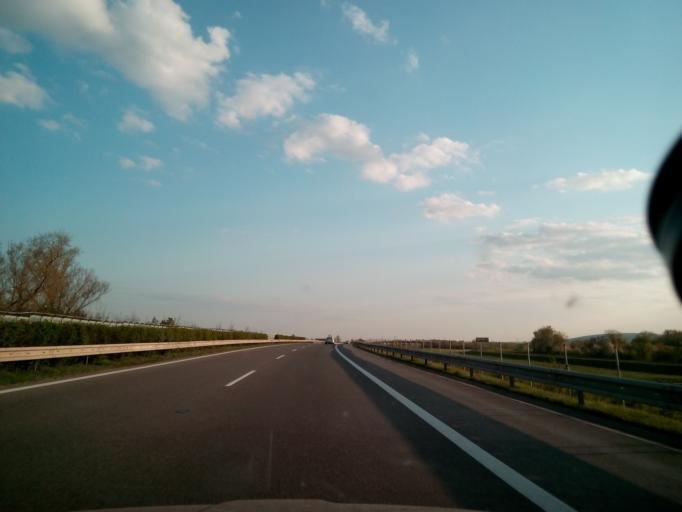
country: SK
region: Trenciansky
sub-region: Okres Nove Mesto nad Vahom
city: Nove Mesto nad Vahom
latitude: 48.7913
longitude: 17.8880
